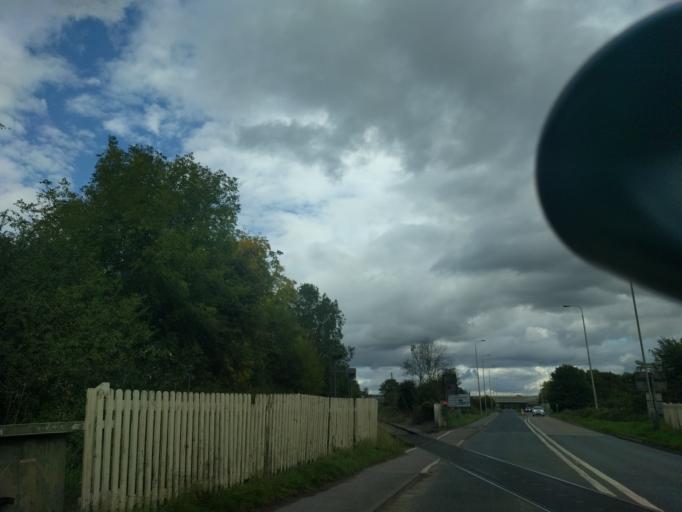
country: GB
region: England
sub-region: North Yorkshire
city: Bedale
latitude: 54.2986
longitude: -1.5707
